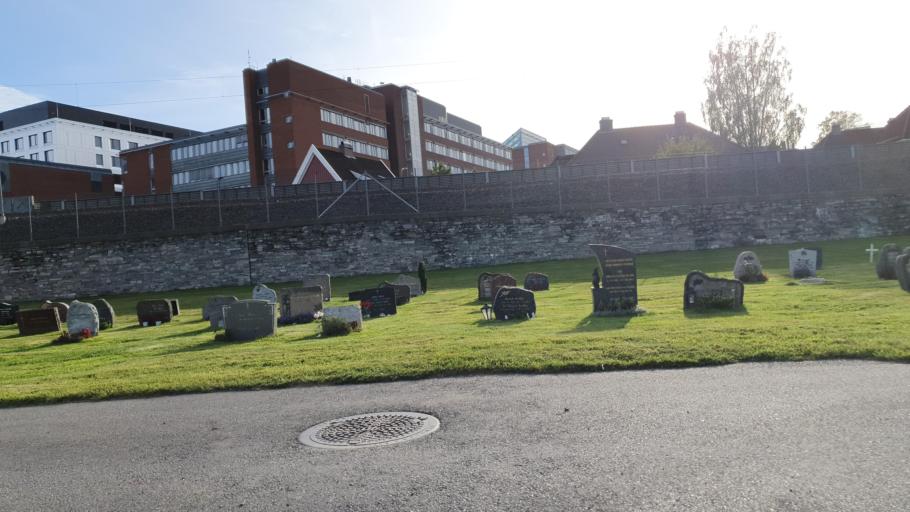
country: NO
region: Vestfold
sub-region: Tonsberg
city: Tonsberg
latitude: 59.2741
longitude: 10.4202
